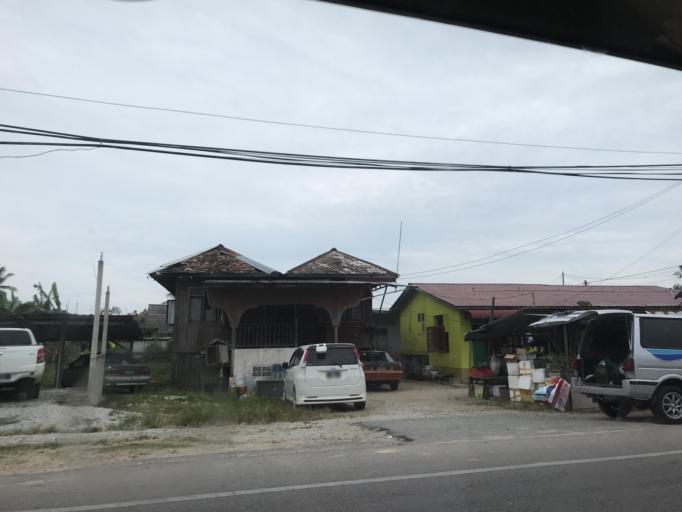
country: MY
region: Kelantan
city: Kota Bharu
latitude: 6.1434
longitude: 102.2184
